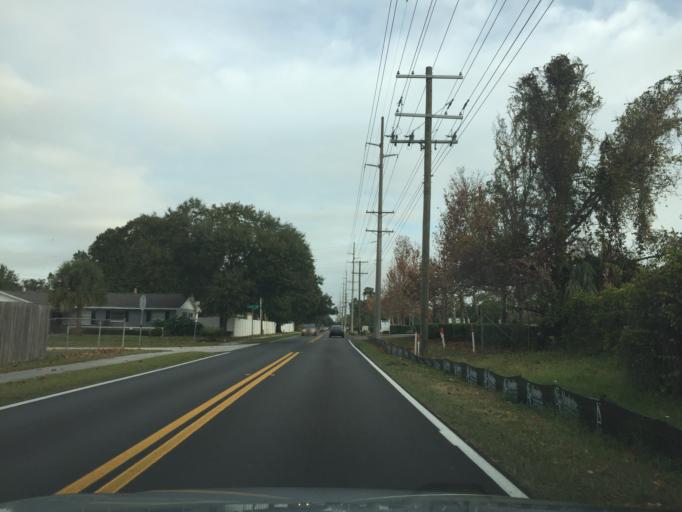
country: US
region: Florida
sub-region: Hillsborough County
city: Town 'n' Country
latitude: 27.9841
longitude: -82.5505
